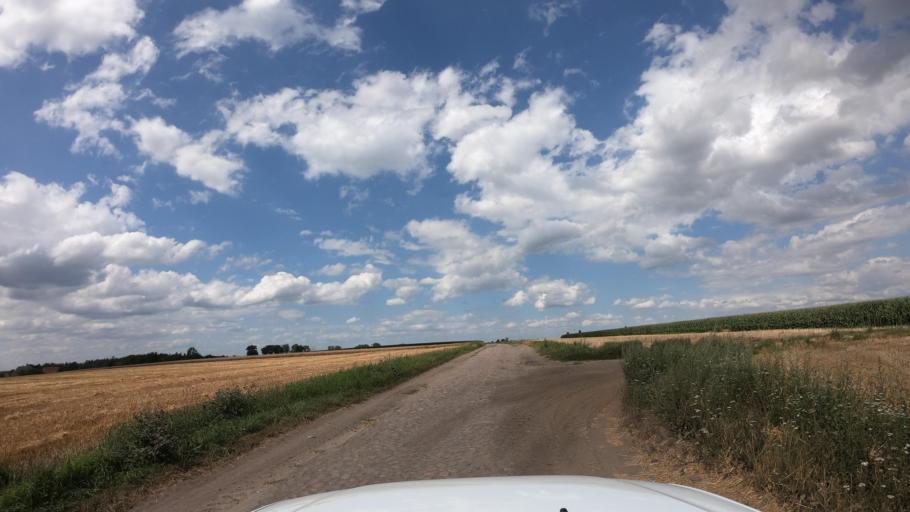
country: PL
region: West Pomeranian Voivodeship
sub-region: Powiat pyrzycki
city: Warnice
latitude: 53.2416
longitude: 14.9135
